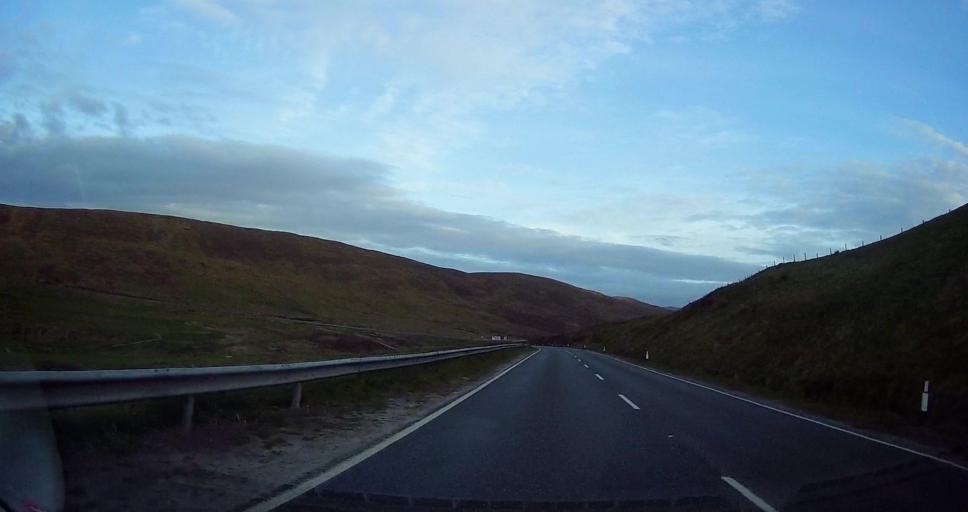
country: GB
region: Scotland
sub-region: Shetland Islands
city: Lerwick
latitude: 60.1656
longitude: -1.2279
